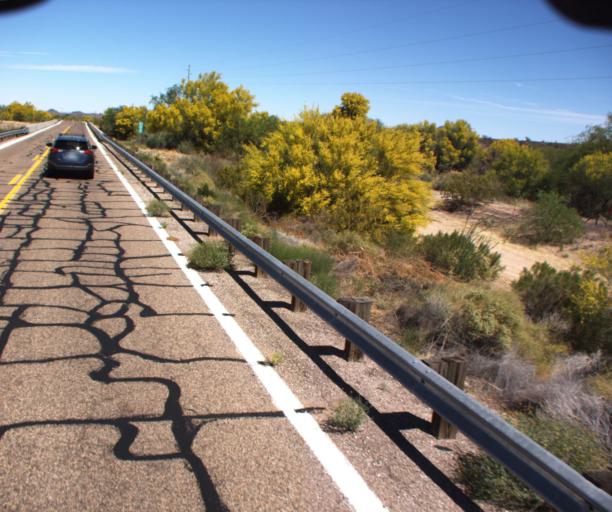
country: US
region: Arizona
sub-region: Pima County
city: Ajo
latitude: 32.4982
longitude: -112.8815
